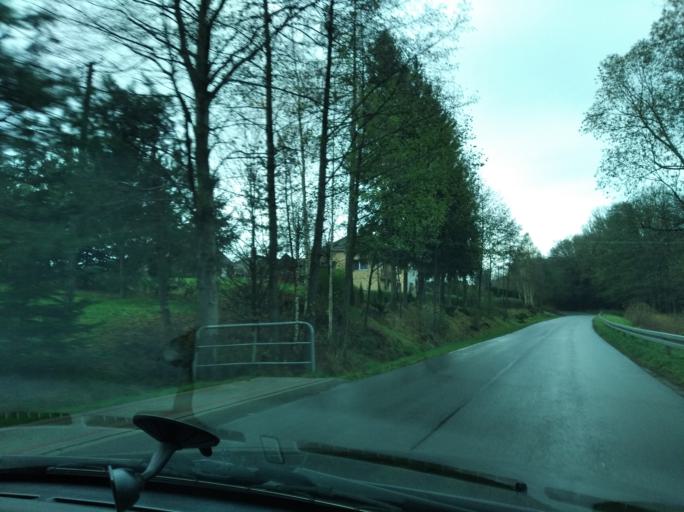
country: PL
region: Subcarpathian Voivodeship
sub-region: Powiat rzeszowski
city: Lecka
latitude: 49.9007
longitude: 22.0146
